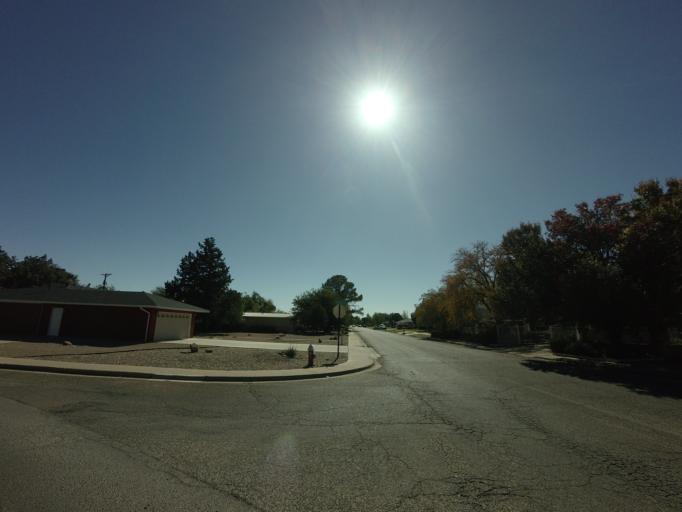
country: US
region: New Mexico
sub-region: Curry County
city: Clovis
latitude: 34.4267
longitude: -103.2002
